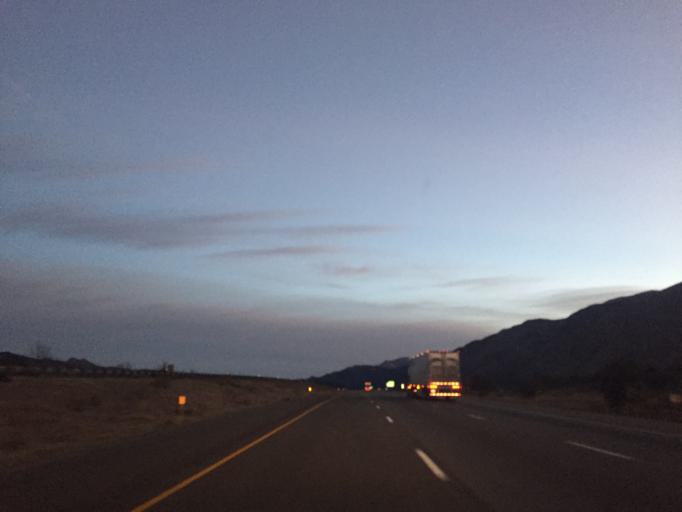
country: US
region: Utah
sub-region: Washington County
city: Toquerville
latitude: 37.3157
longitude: -113.2923
